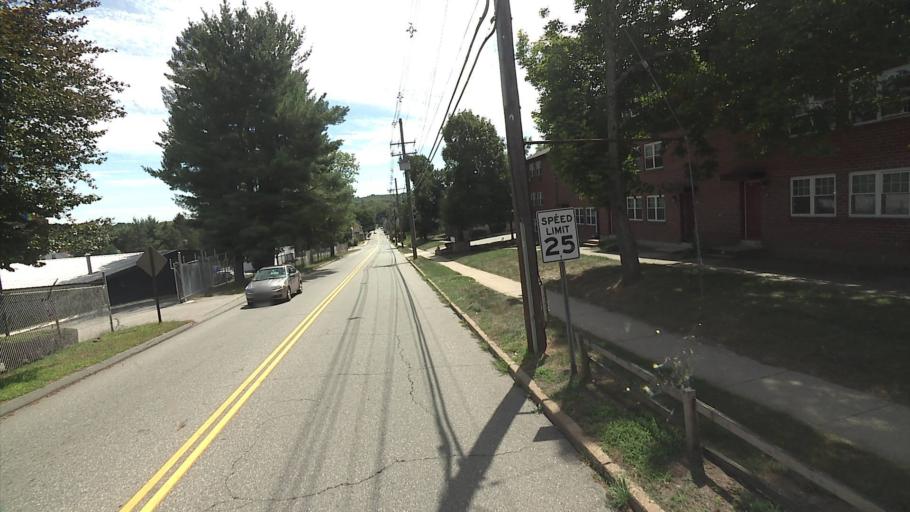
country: US
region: Connecticut
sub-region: Windham County
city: Willimantic
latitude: 41.7186
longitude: -72.1992
